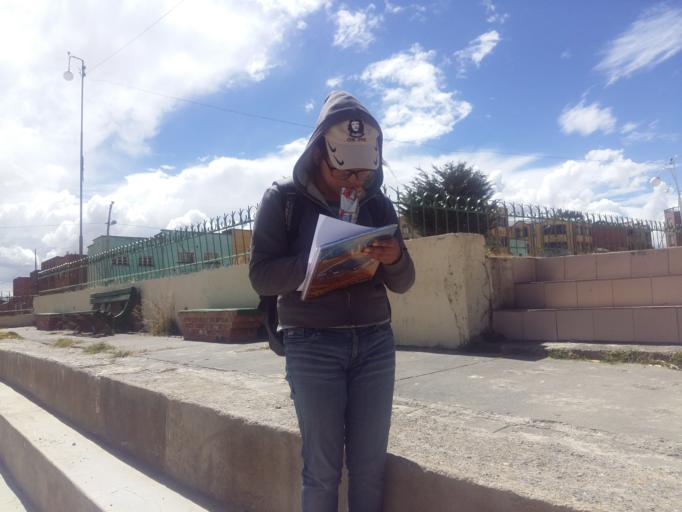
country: BO
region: La Paz
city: Batallas
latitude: -16.2848
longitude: -68.6010
